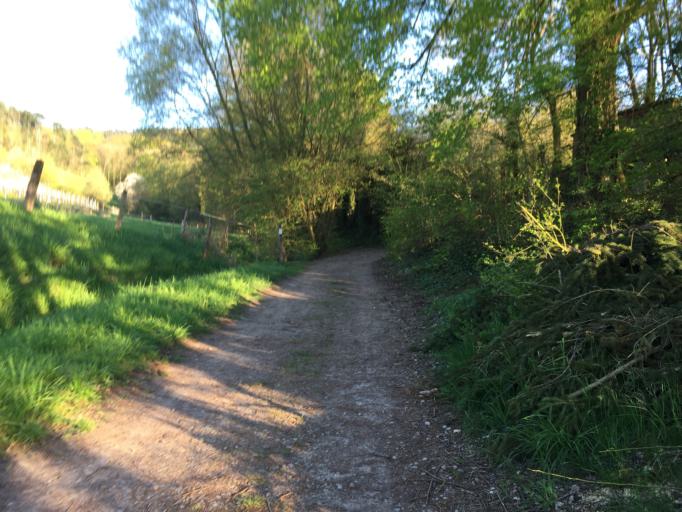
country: DE
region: Baden-Wuerttemberg
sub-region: Karlsruhe Region
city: Schriesheim
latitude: 49.5048
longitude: 8.6695
